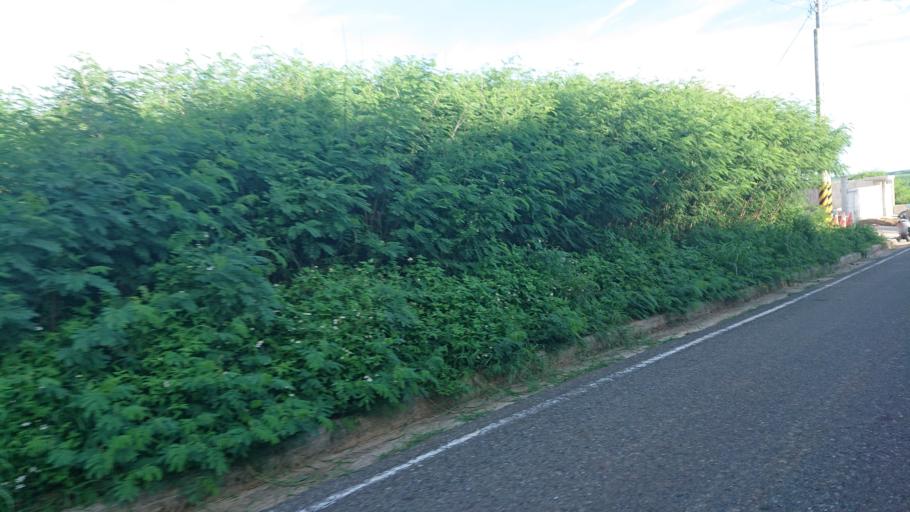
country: TW
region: Taiwan
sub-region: Penghu
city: Ma-kung
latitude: 23.5969
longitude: 119.5167
